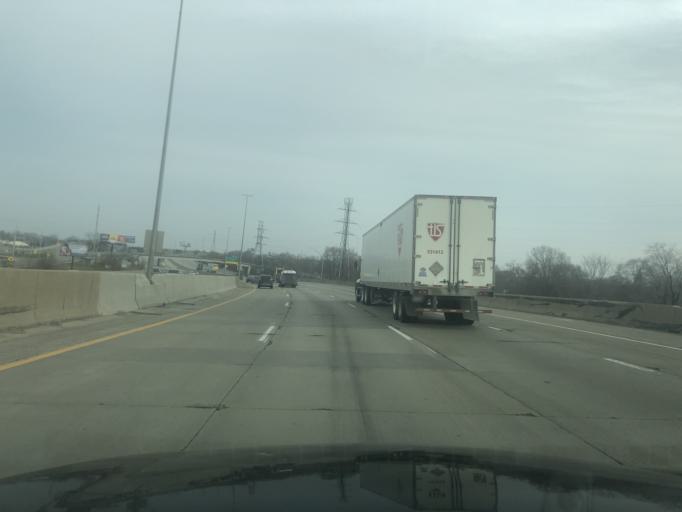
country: US
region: Michigan
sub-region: Wayne County
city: River Rouge
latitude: 42.2783
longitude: -83.1523
